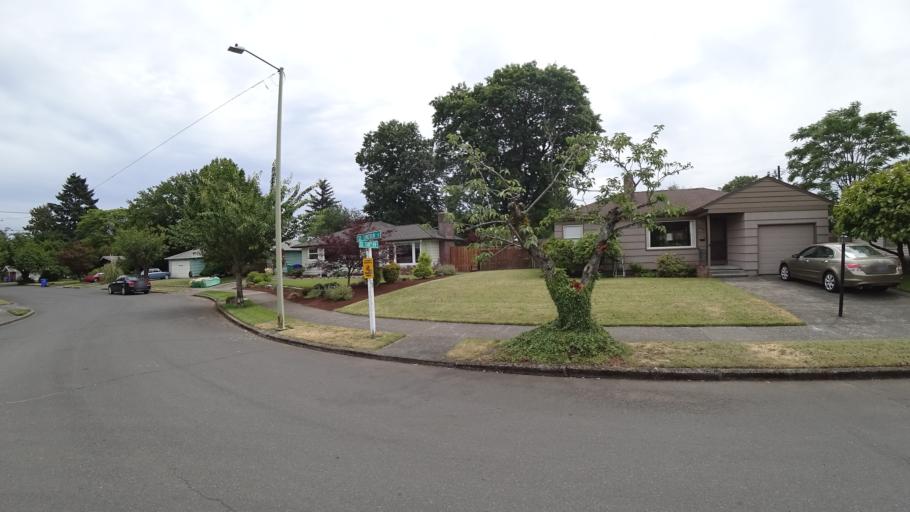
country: US
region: Oregon
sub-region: Multnomah County
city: Lents
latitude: 45.5081
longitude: -122.5607
